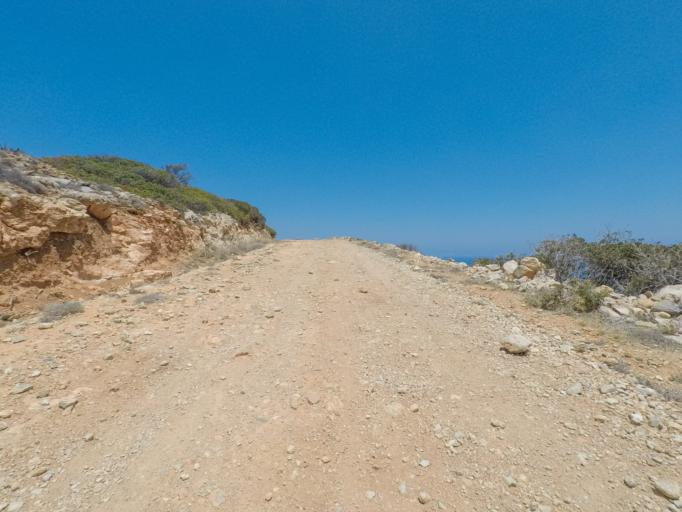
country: GR
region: Crete
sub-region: Nomos Lasithiou
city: Elounda
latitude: 35.3239
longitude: 25.7606
